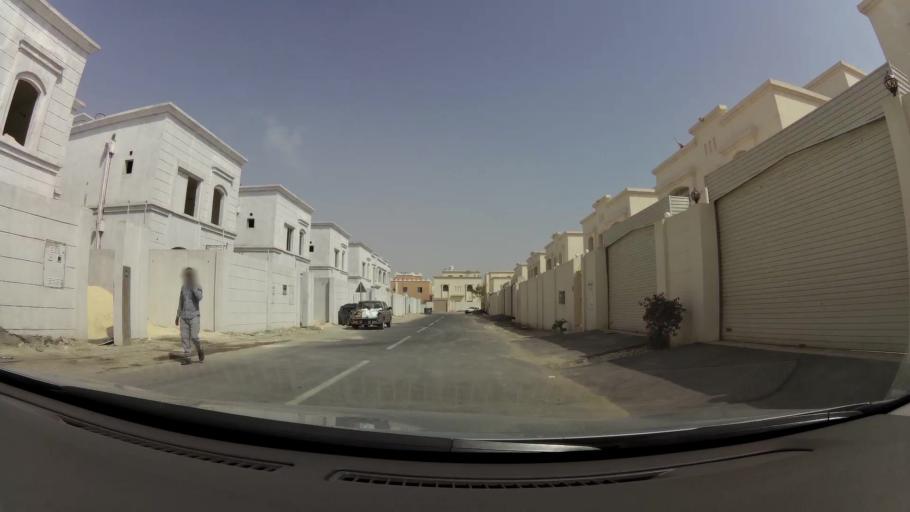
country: QA
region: Baladiyat ad Dawhah
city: Doha
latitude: 25.3048
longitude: 51.4794
